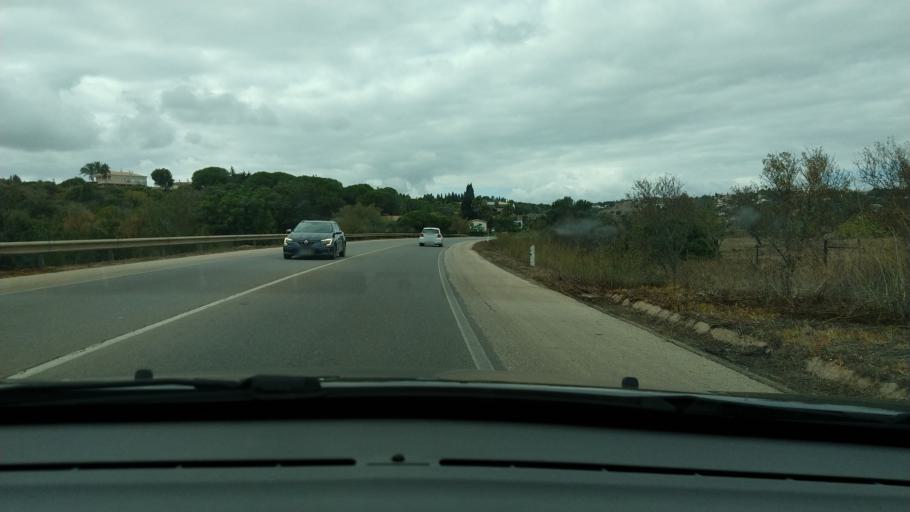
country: PT
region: Faro
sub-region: Lagos
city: Lagos
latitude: 37.1024
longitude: -8.7002
